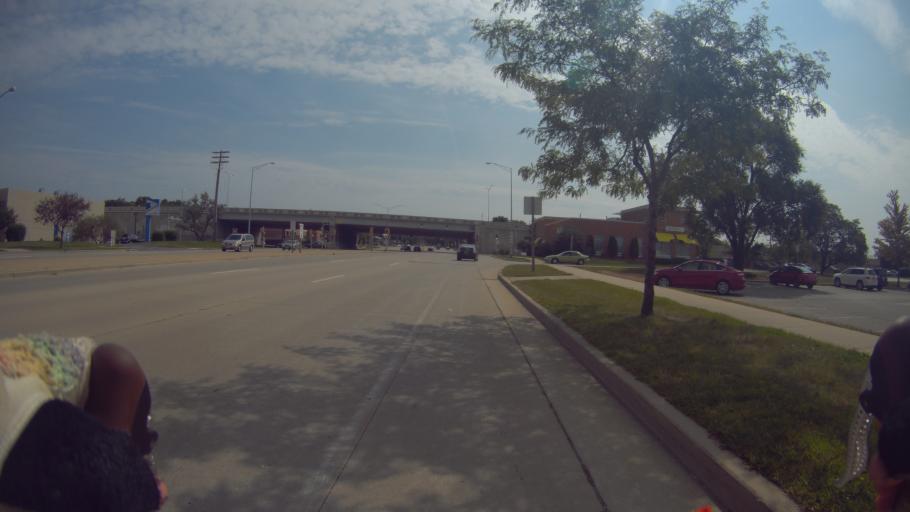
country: US
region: Wisconsin
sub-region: Dane County
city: Monona
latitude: 43.0982
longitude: -89.3180
